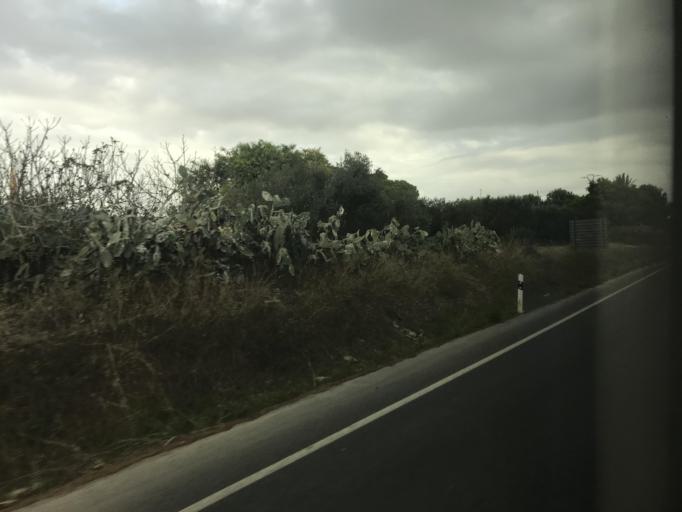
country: ES
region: Valencia
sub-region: Provincia de Alicante
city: Guardamar del Segura
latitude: 38.1278
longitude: -0.6505
